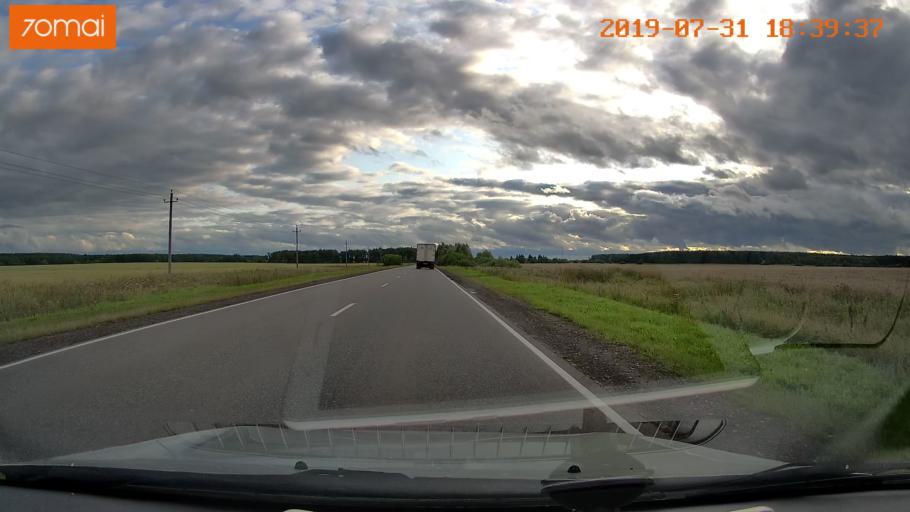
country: RU
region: Moskovskaya
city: Voskresensk
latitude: 55.2661
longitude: 38.6428
